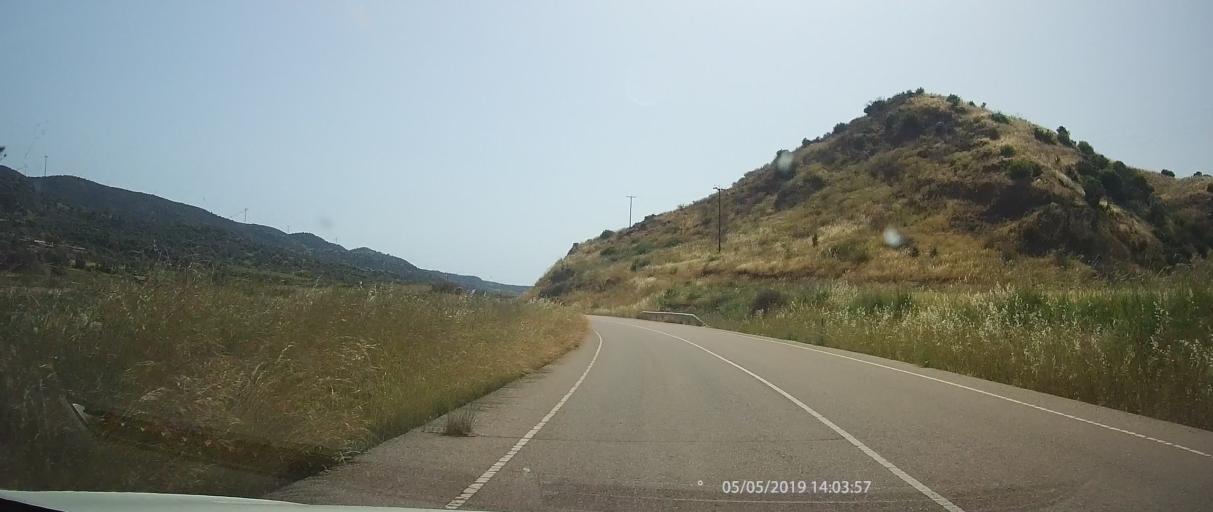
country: CY
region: Limassol
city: Pissouri
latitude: 34.7631
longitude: 32.6306
